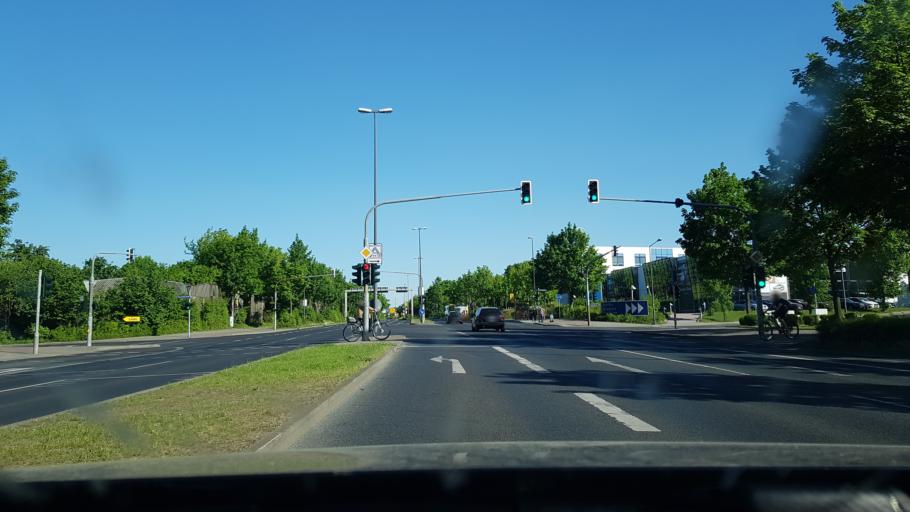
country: DE
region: Saxony
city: Kreischa
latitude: 51.0021
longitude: 13.7932
